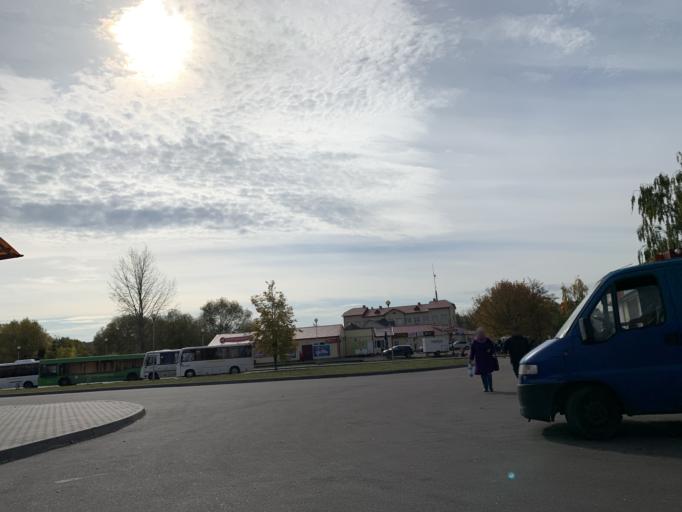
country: BY
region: Minsk
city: Nyasvizh
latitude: 53.2211
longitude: 26.6745
